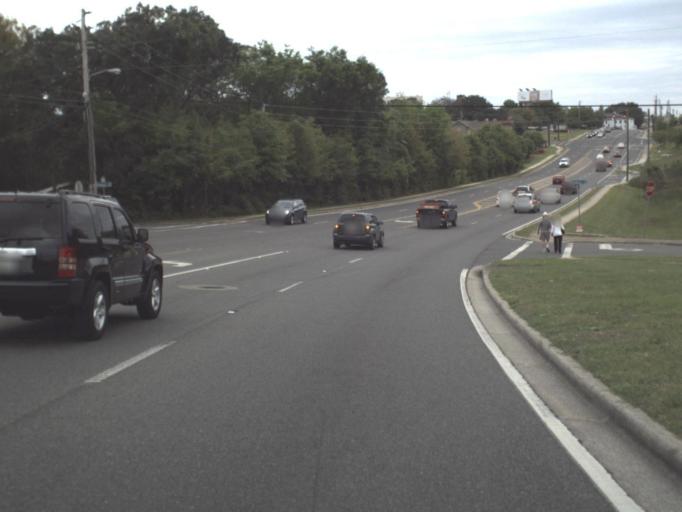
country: US
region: Florida
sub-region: Escambia County
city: Brent
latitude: 30.4753
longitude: -87.2193
